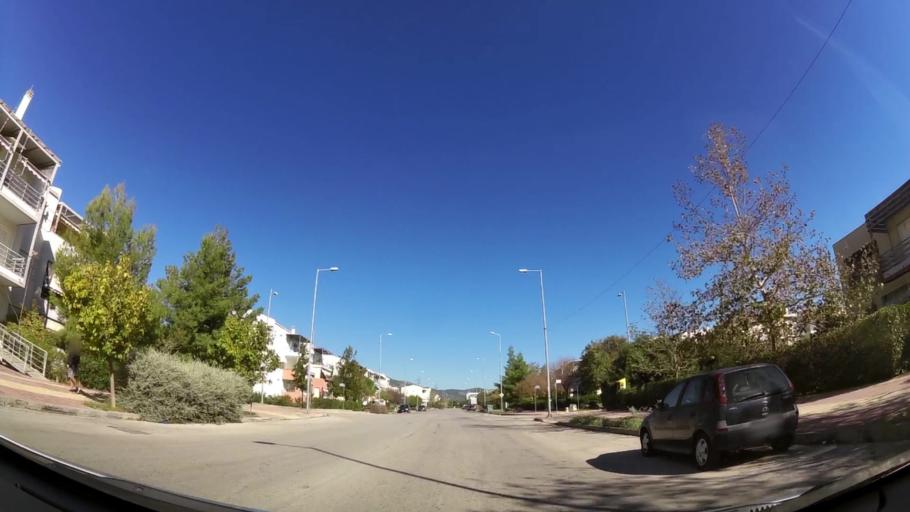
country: GR
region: Attica
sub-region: Nomarchia Anatolikis Attikis
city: Thrakomakedones
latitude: 38.1120
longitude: 23.7707
